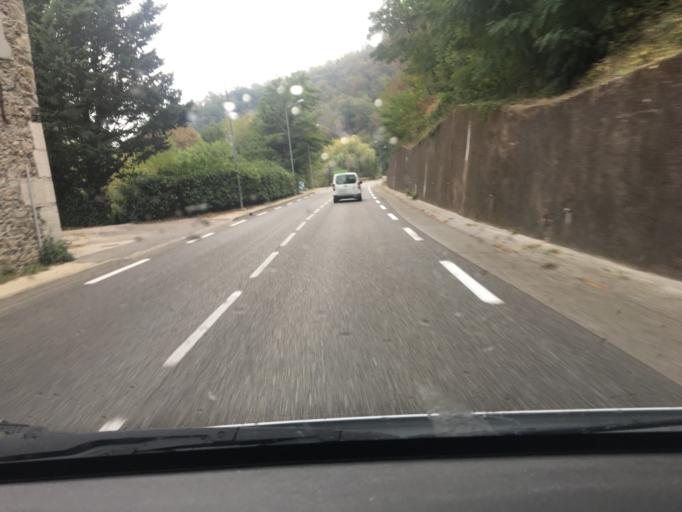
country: FR
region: Rhone-Alpes
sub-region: Departement de l'Ardeche
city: Saint-Jean-de-Muzols
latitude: 45.0650
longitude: 4.7890
